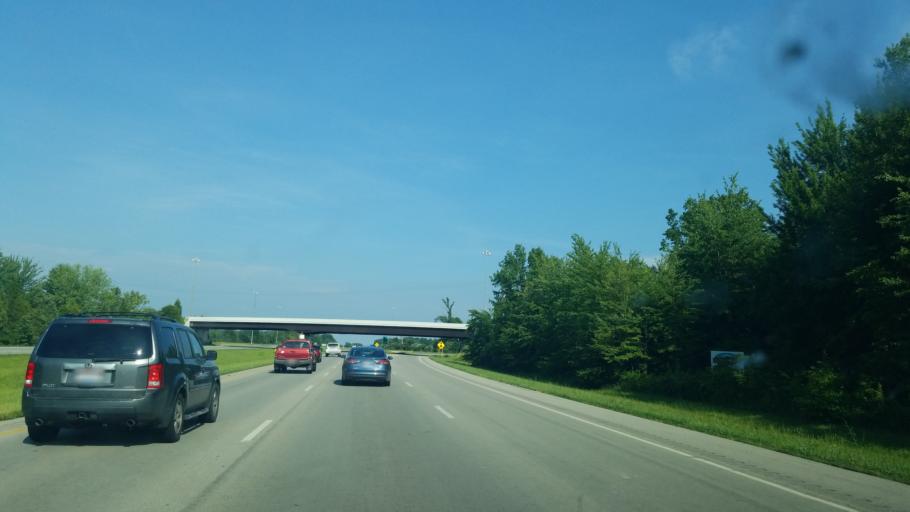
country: US
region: Ohio
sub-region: Clermont County
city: Batavia
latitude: 39.0763
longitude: -84.1236
